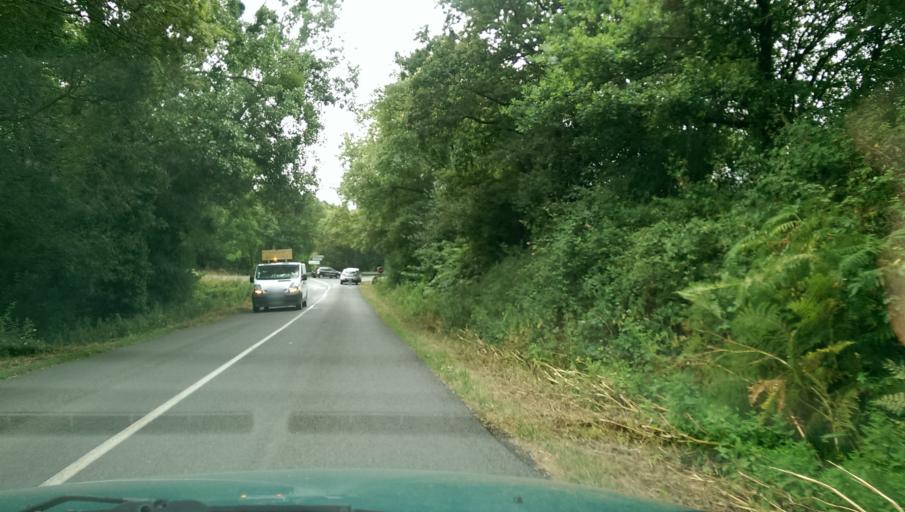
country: FR
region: Pays de la Loire
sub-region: Departement de la Loire-Atlantique
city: Aigrefeuille-sur-Maine
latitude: 47.0715
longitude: -1.3863
